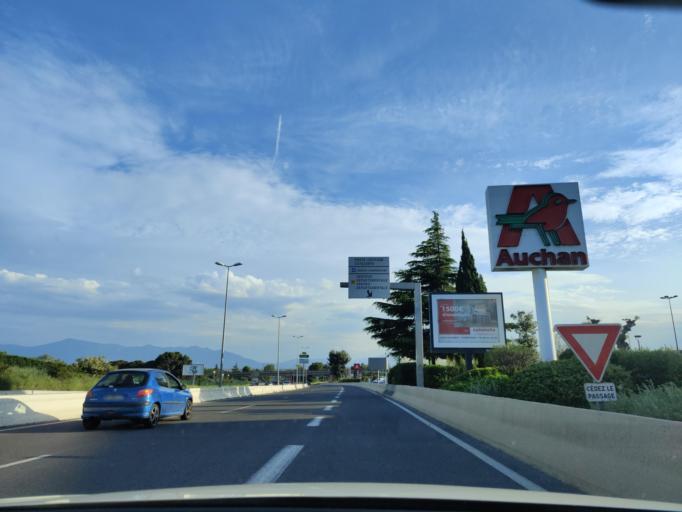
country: FR
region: Languedoc-Roussillon
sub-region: Departement des Pyrenees-Orientales
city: Perpignan
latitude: 42.6700
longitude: 2.8850
